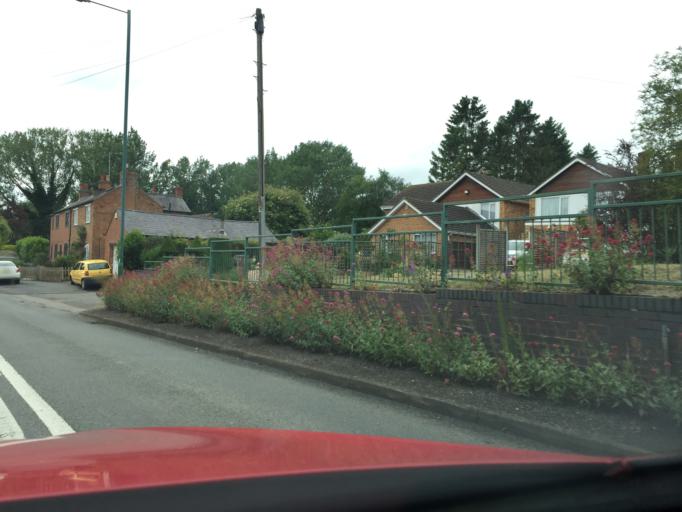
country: GB
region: England
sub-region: Warwickshire
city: Southam
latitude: 52.2506
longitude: -1.3885
